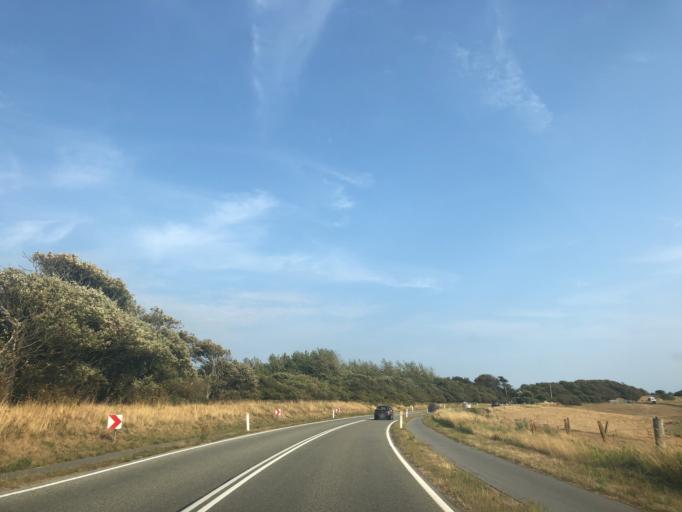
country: DK
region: North Denmark
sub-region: Morso Kommune
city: Nykobing Mors
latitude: 56.7944
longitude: 9.0395
